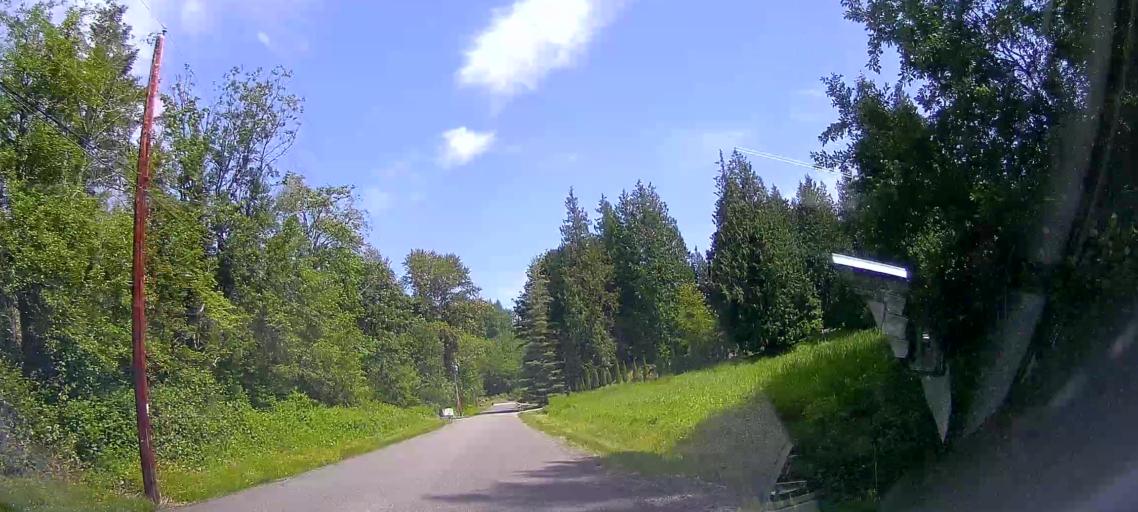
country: US
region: Washington
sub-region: Skagit County
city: Mount Vernon
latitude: 48.4064
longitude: -122.3000
